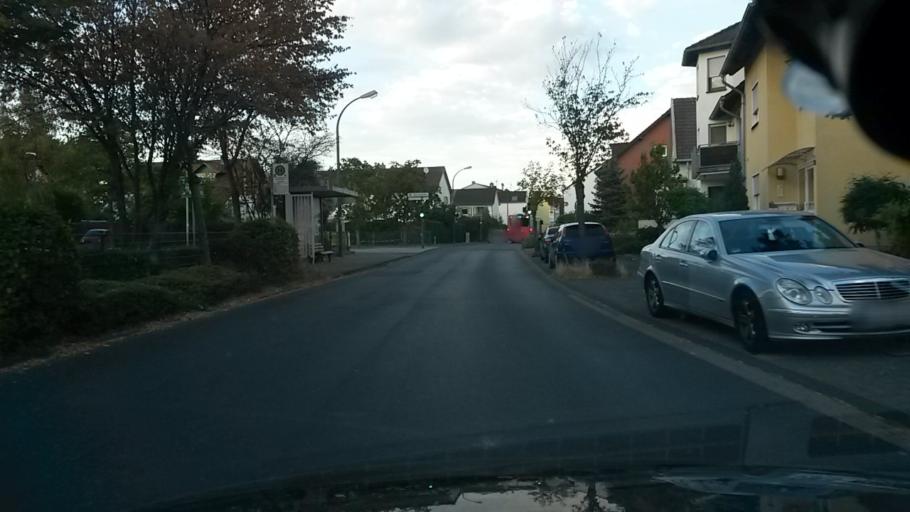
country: DE
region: North Rhine-Westphalia
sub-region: Regierungsbezirk Koln
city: Alfter
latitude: 50.7225
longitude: 7.0400
